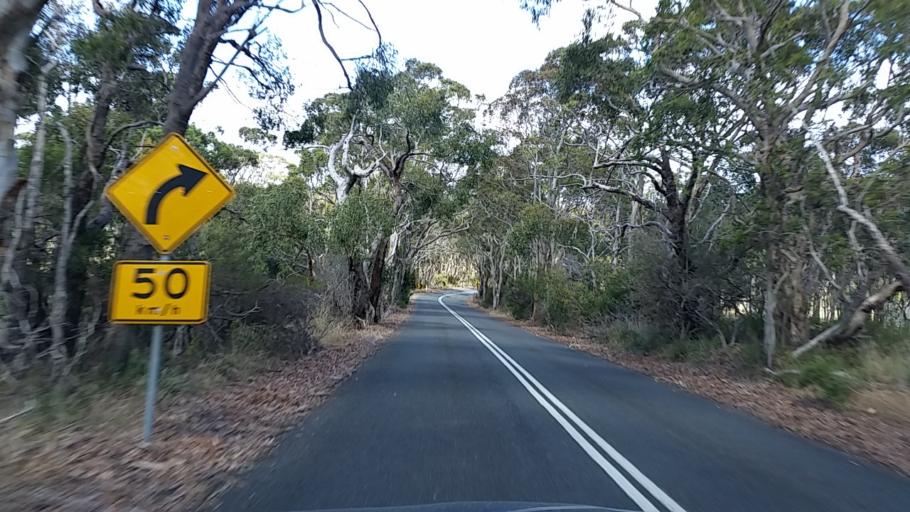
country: AU
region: South Australia
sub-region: Alexandrina
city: Port Elliot
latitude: -35.4658
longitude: 138.6567
